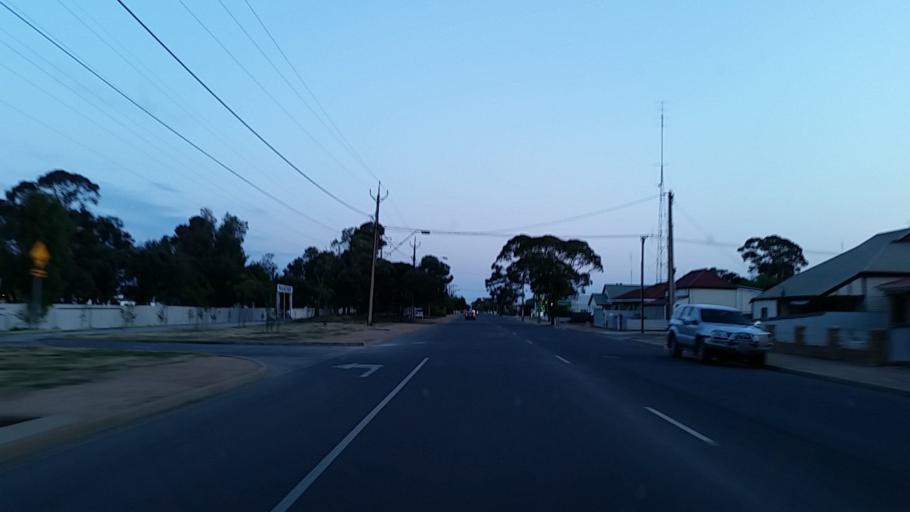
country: AU
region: South Australia
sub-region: Port Pirie City and Dists
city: Port Pirie
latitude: -33.1860
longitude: 138.0039
